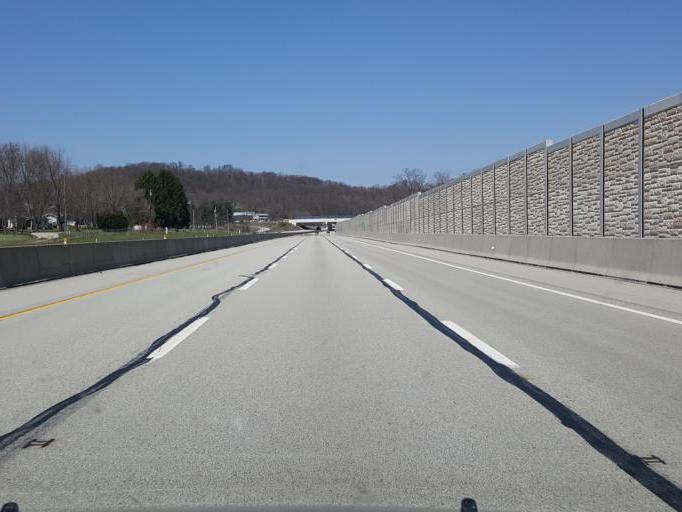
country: US
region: Pennsylvania
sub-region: Westmoreland County
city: New Stanton
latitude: 40.2465
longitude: -79.6385
